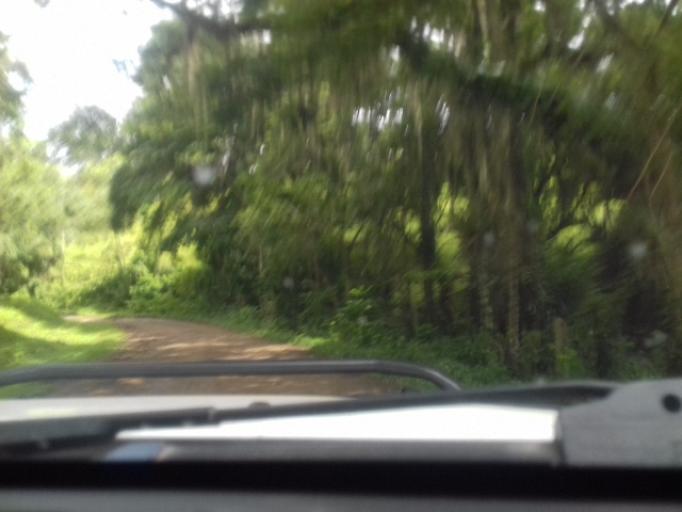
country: NI
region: Matagalpa
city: Matiguas
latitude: 12.8711
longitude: -85.3847
